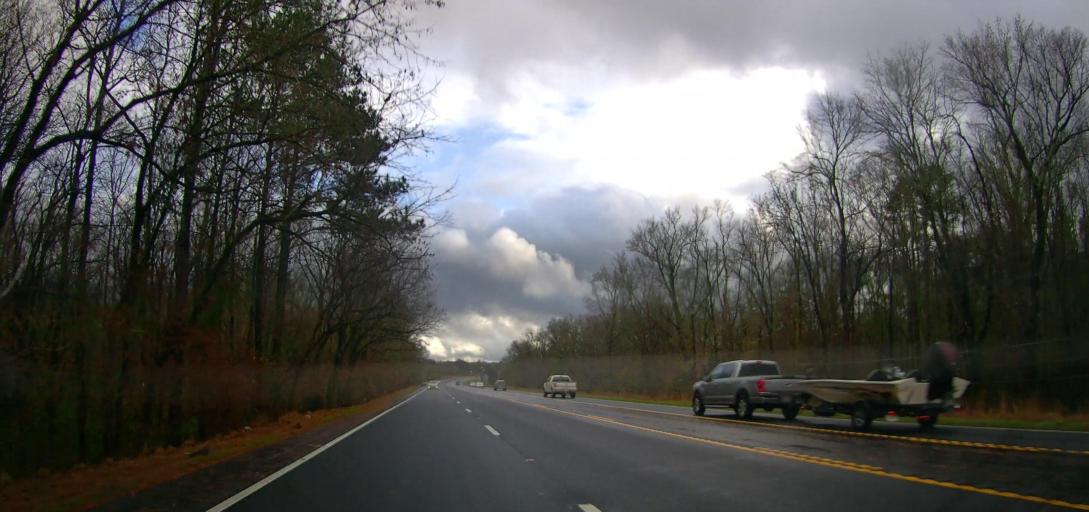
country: US
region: Georgia
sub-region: Clarke County
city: Athens
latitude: 33.9886
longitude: -83.3779
